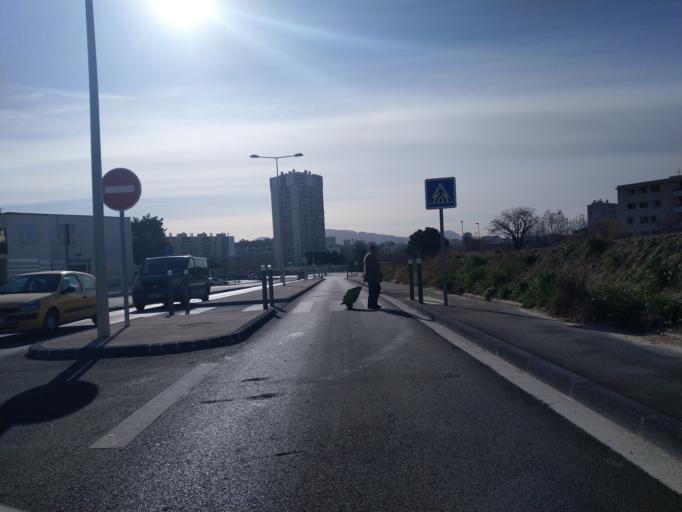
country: FR
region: Provence-Alpes-Cote d'Azur
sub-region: Departement des Bouches-du-Rhone
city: Marseille 14
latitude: 43.3317
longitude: 5.3869
